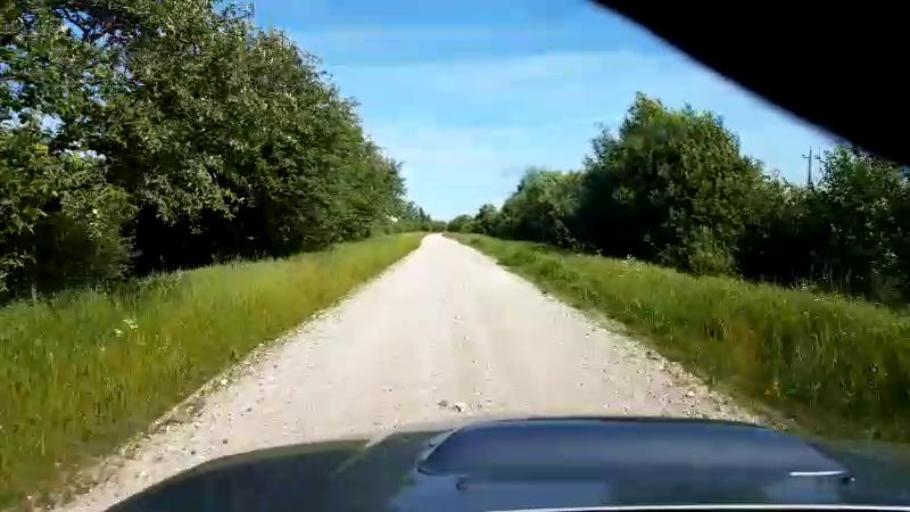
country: EE
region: Paernumaa
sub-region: Sauga vald
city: Sauga
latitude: 58.4707
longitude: 24.5334
